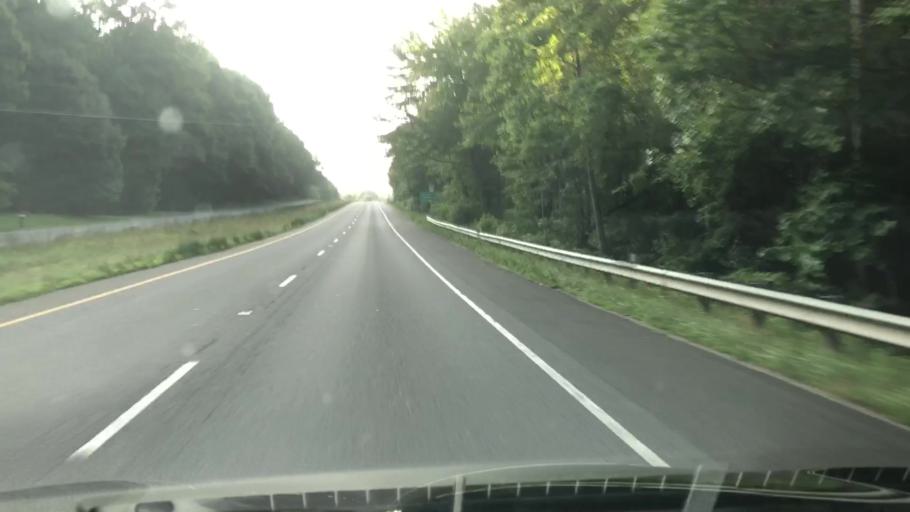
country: US
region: Virginia
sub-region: Stafford County
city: Falmouth
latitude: 38.4039
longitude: -77.5772
